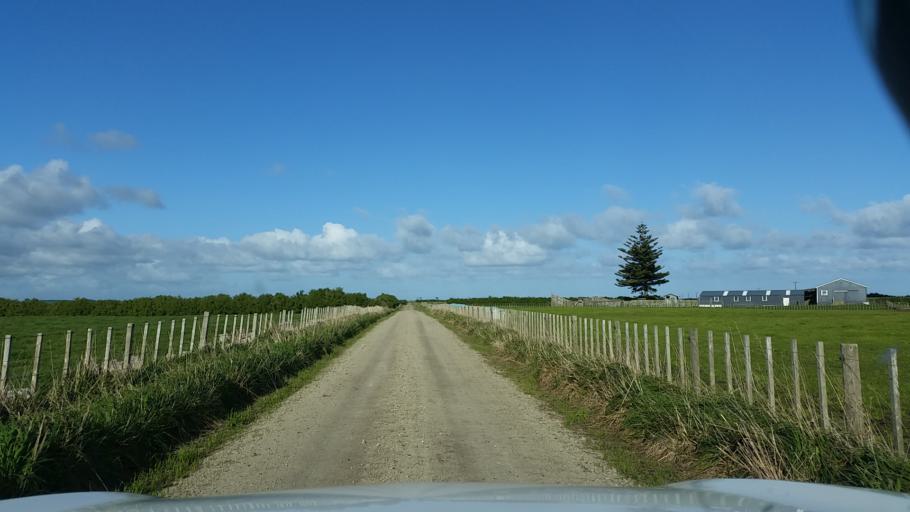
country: NZ
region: Taranaki
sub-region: South Taranaki District
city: Patea
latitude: -39.7474
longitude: 174.5168
